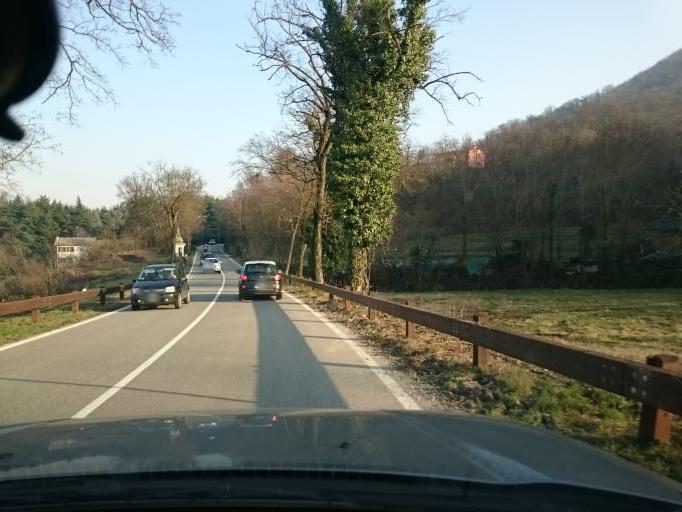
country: IT
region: Veneto
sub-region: Provincia di Padova
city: Treponti
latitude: 45.3300
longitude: 11.6883
